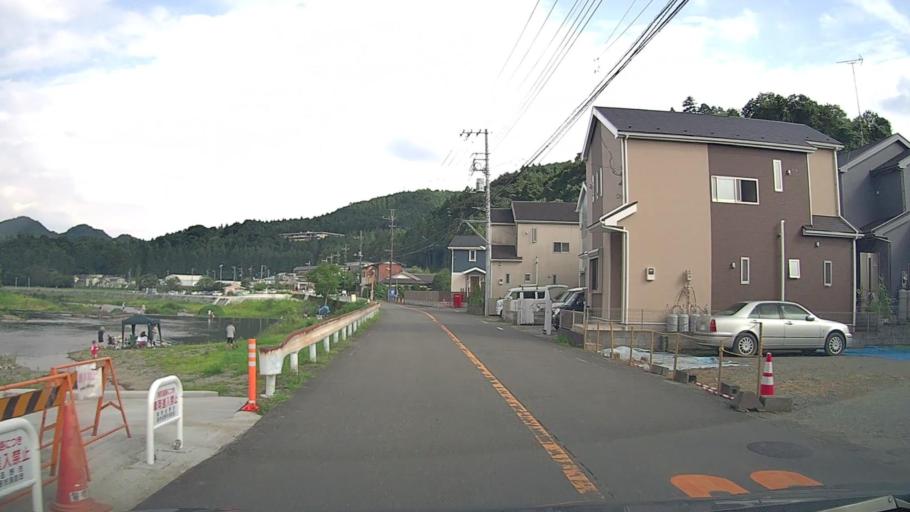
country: JP
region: Tokyo
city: Itsukaichi
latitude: 35.7236
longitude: 139.2224
